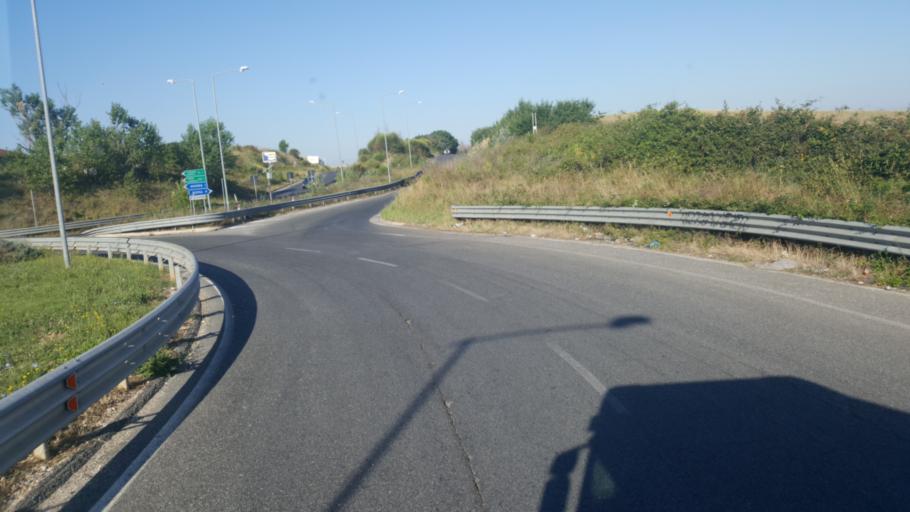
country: IT
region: Latium
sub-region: Citta metropolitana di Roma Capitale
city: Albuccione
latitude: 41.9704
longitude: 12.6882
